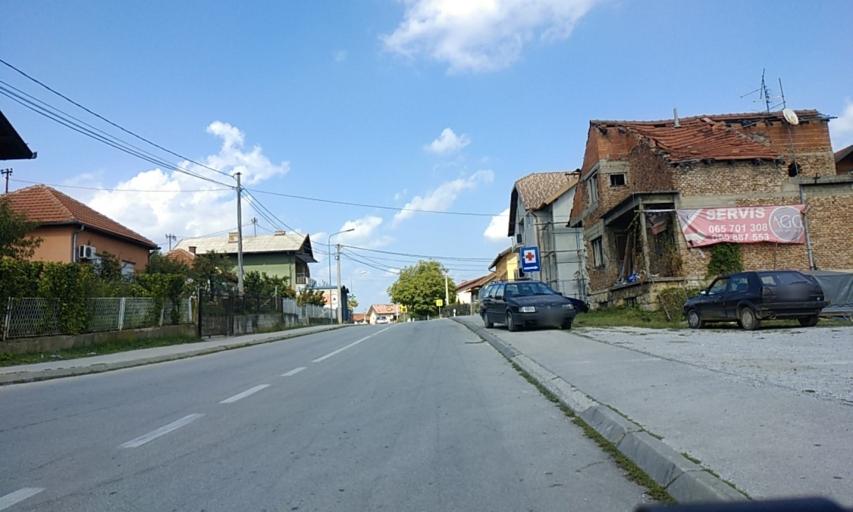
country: BA
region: Republika Srpska
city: Banja Luka
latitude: 44.7856
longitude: 17.1939
